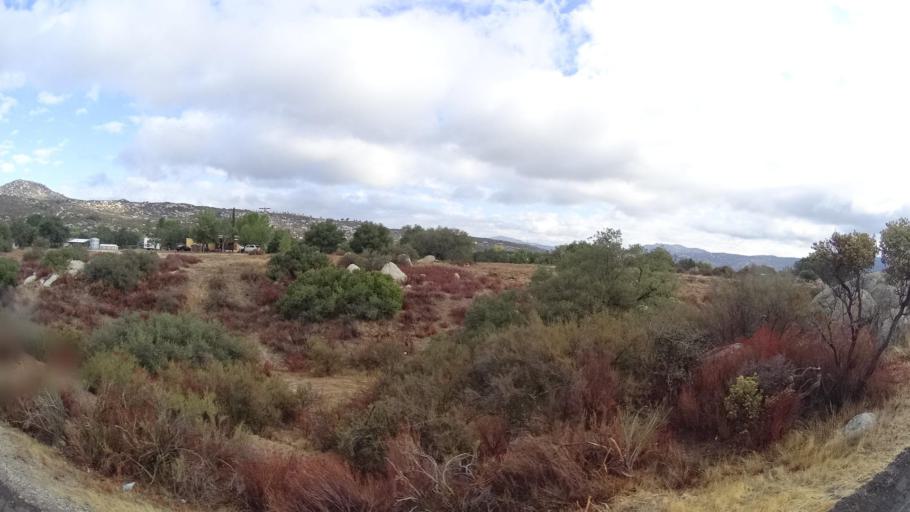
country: MX
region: Baja California
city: Tecate
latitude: 32.6266
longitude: -116.6053
